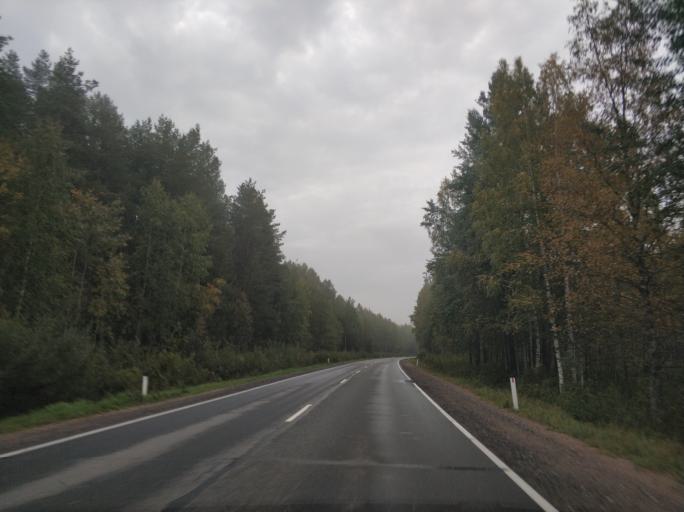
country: RU
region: Leningrad
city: Shcheglovo
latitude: 60.0999
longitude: 30.8353
